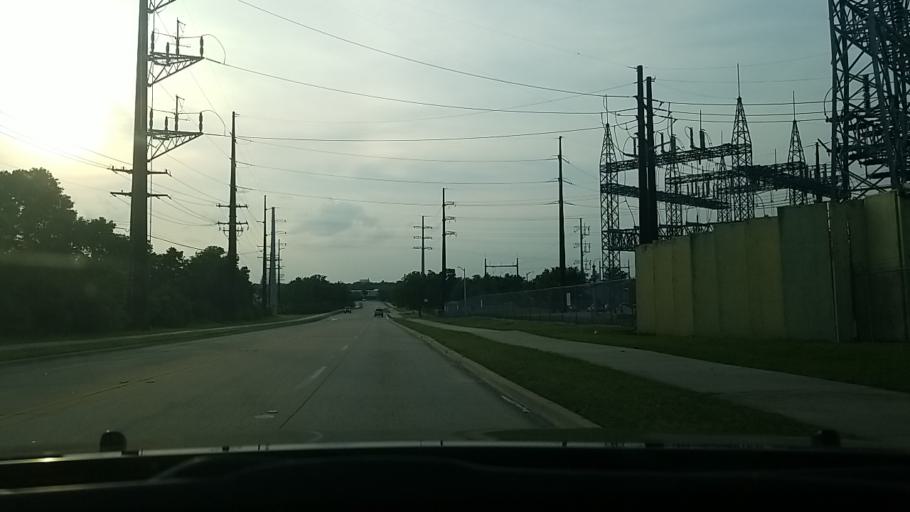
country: US
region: Texas
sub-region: Denton County
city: Denton
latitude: 33.1971
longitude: -97.1074
